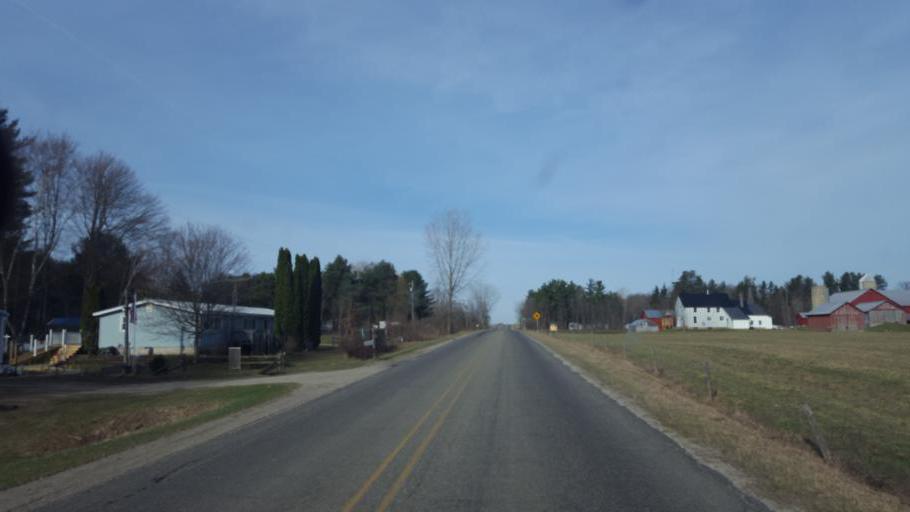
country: US
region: Michigan
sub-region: Montcalm County
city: Howard City
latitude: 43.5259
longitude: -85.4785
